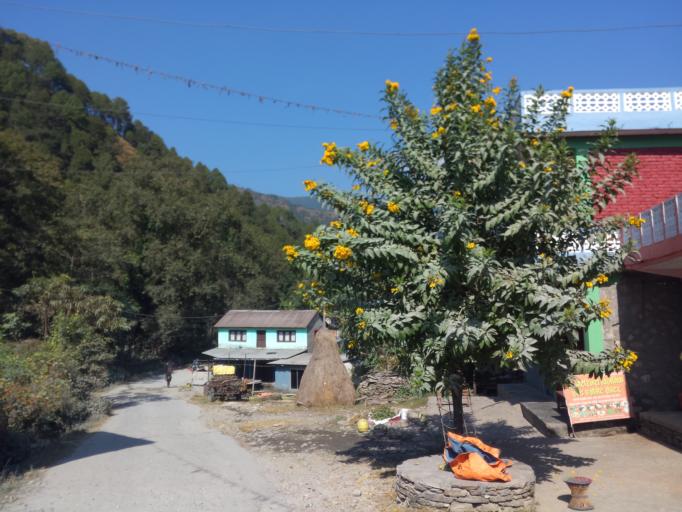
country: NP
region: Western Region
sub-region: Gandaki Zone
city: Pokhara
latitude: 28.2713
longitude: 83.9801
